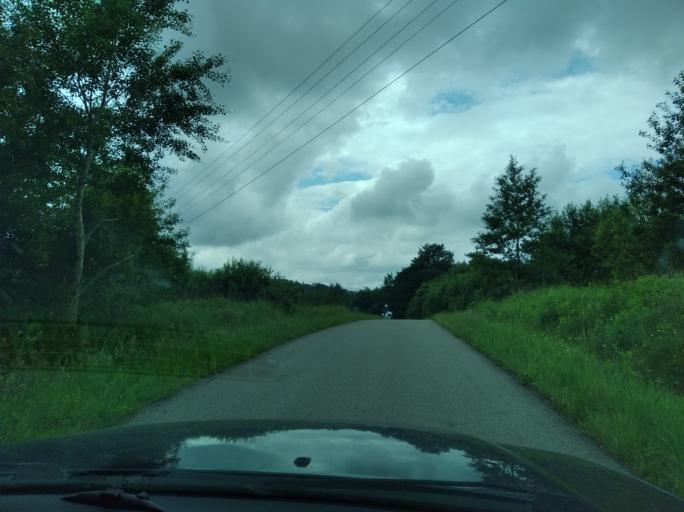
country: PL
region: Subcarpathian Voivodeship
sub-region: Powiat przemyski
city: Przedmiescie Dubieckie
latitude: 49.8778
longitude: 22.4056
